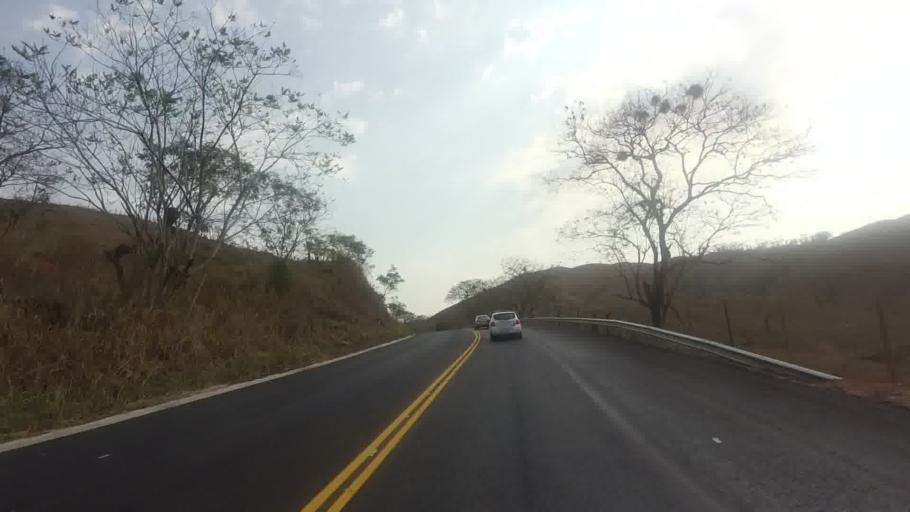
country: BR
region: Rio de Janeiro
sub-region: Bom Jesus Do Itabapoana
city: Bom Jesus do Itabapoana
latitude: -21.2140
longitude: -41.7347
